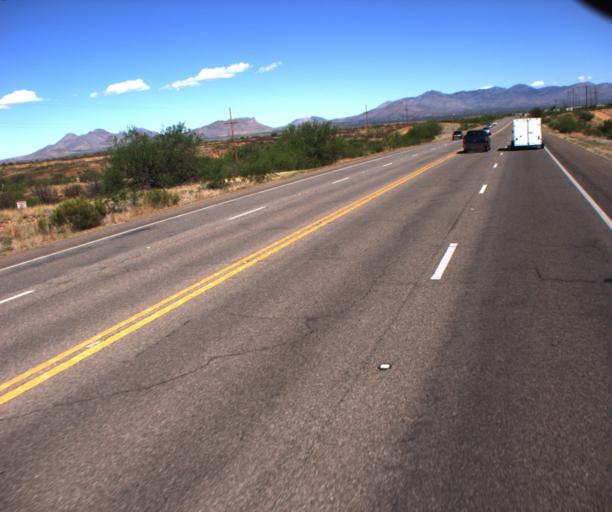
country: US
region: Arizona
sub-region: Cochise County
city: Huachuca City
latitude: 31.6095
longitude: -110.3315
